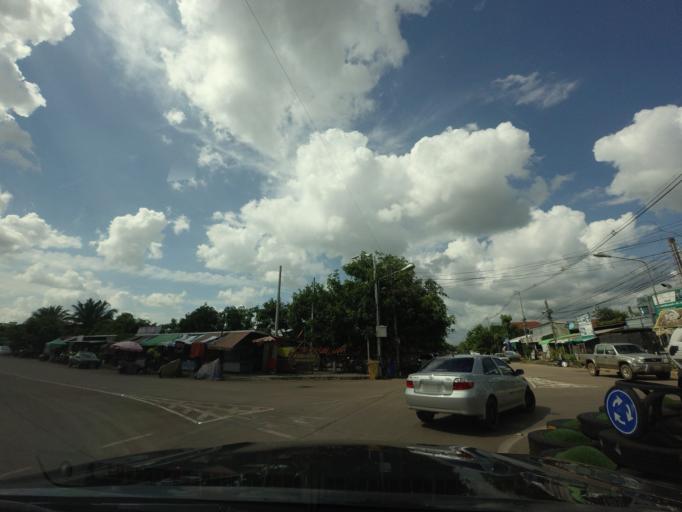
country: TH
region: Changwat Udon Thani
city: Udon Thani
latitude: 17.4153
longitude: 102.7770
